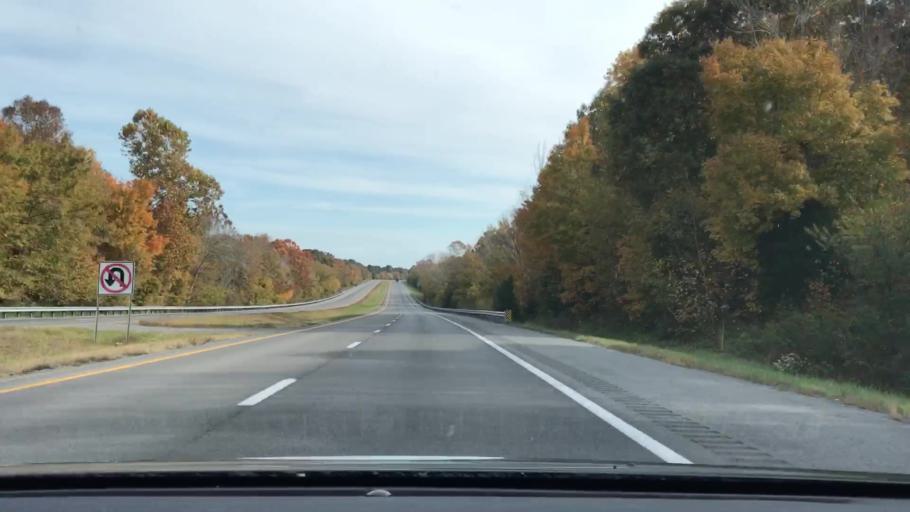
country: US
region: Kentucky
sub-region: Marshall County
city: Benton
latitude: 36.8406
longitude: -88.4177
